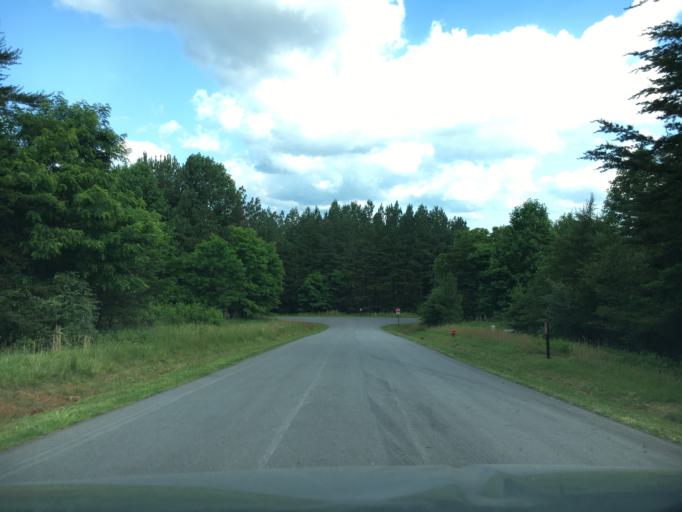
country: US
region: Virginia
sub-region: Bedford County
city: Forest
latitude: 37.3876
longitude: -79.2668
